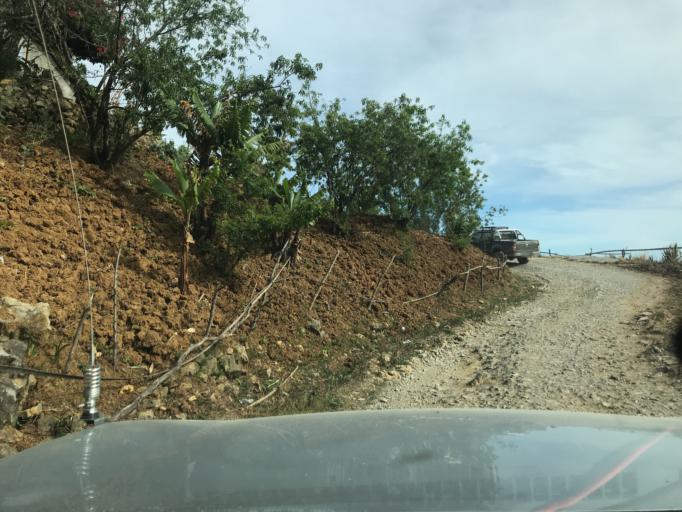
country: TL
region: Manufahi
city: Same
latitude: -8.8778
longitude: 125.5893
